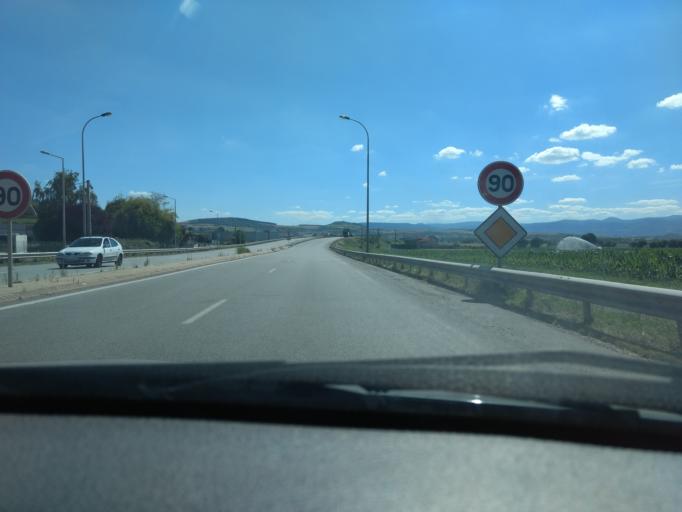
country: FR
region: Auvergne
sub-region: Departement du Puy-de-Dome
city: Dallet
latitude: 45.7915
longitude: 3.2262
